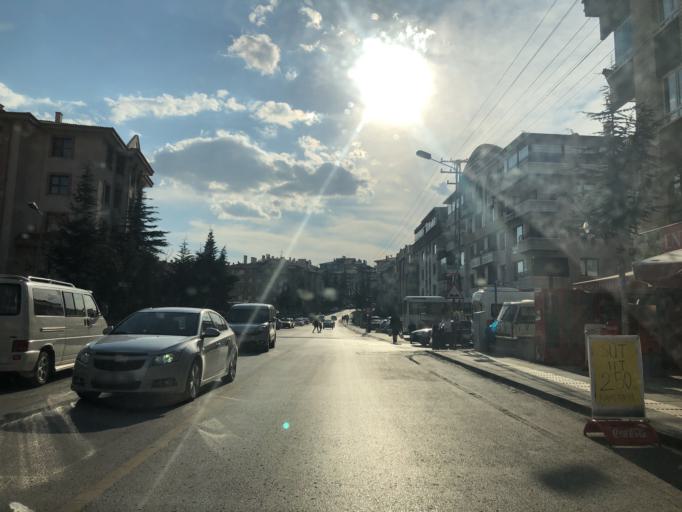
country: TR
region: Ankara
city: Ankara
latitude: 39.9825
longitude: 32.8398
